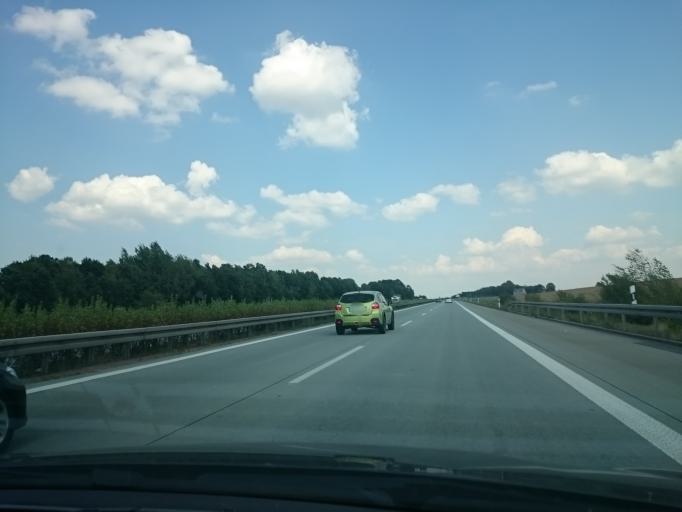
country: DE
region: Saxony
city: Niederdorf
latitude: 50.7515
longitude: 12.7996
